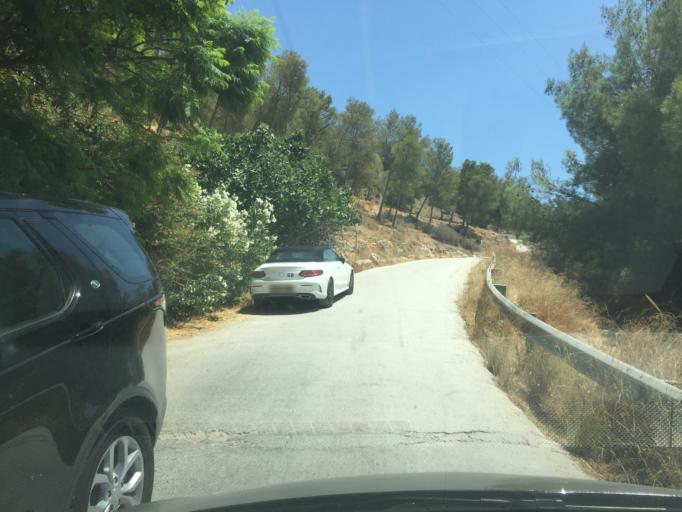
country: ES
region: Andalusia
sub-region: Provincia de Malaga
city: Nerja
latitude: 36.7707
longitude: -3.8779
